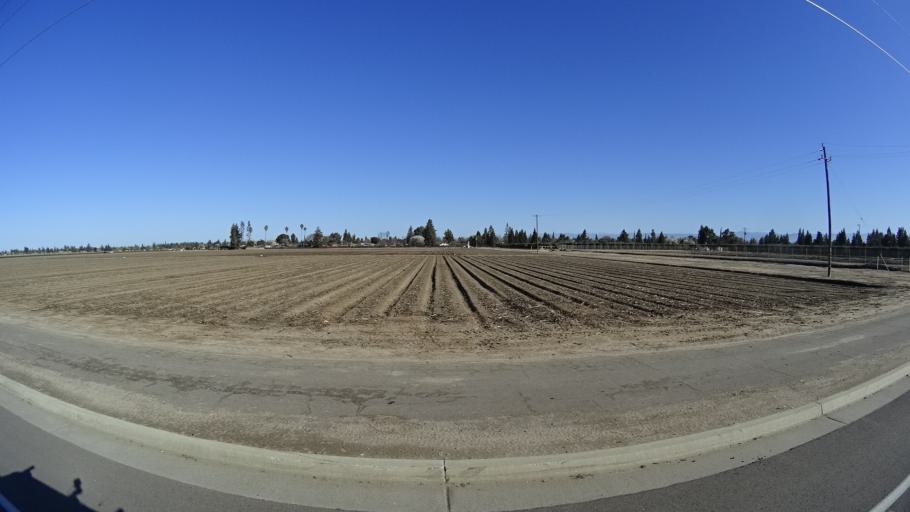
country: US
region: California
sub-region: Fresno County
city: Clovis
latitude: 36.8232
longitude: -119.7333
